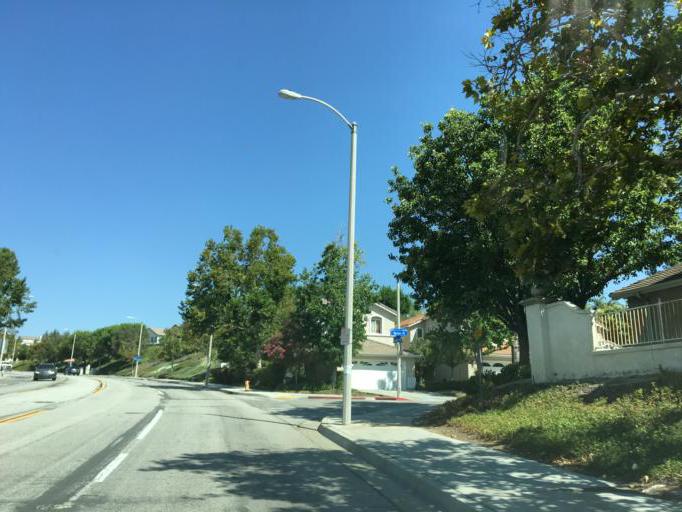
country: US
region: California
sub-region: Los Angeles County
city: Santa Clarita
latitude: 34.3902
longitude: -118.5837
